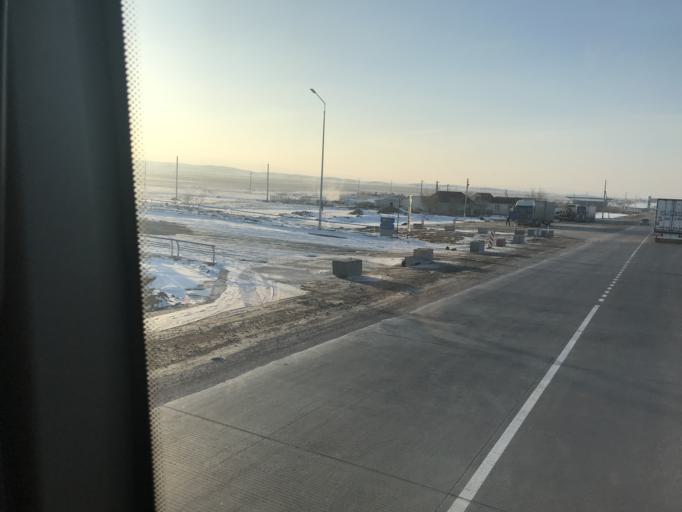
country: KG
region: Chuy
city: Ivanovka
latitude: 43.3995
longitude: 75.1165
